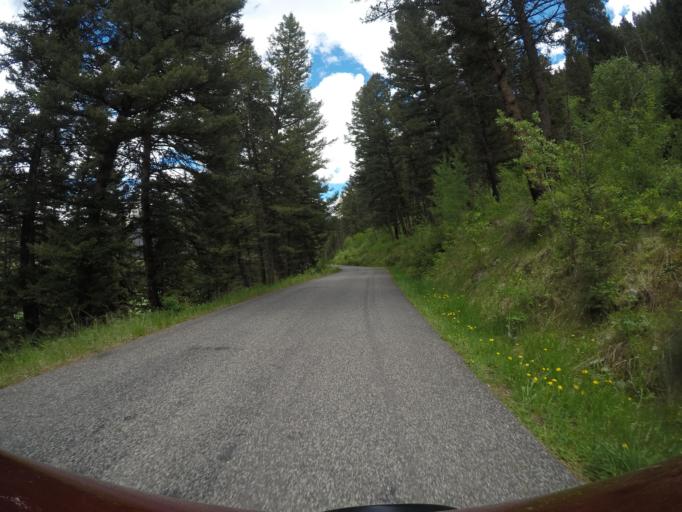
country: US
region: Montana
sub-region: Park County
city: Livingston
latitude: 45.4995
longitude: -110.5372
